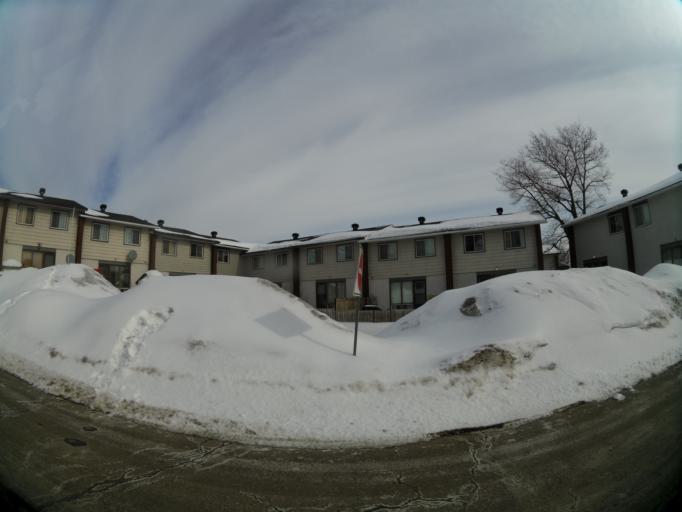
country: CA
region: Ontario
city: Ottawa
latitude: 45.4427
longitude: -75.5987
